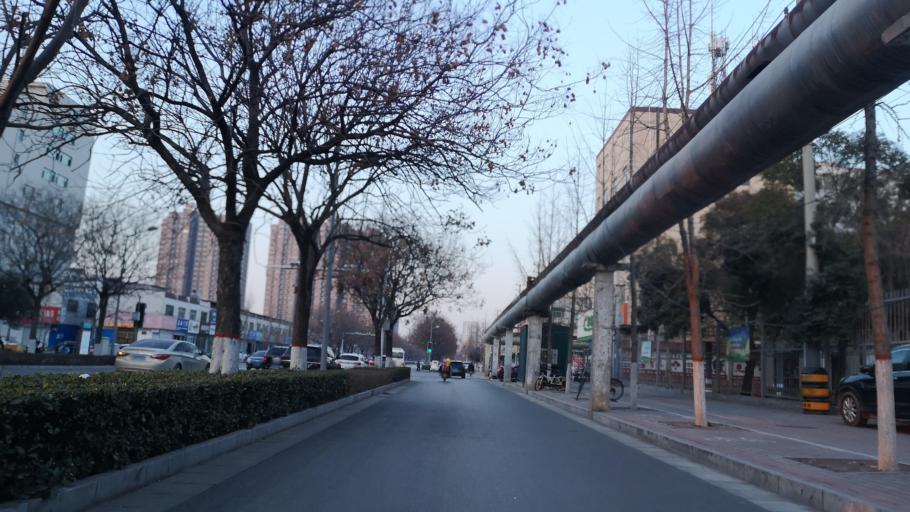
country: CN
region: Henan Sheng
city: Puyang
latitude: 35.7684
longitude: 115.0142
